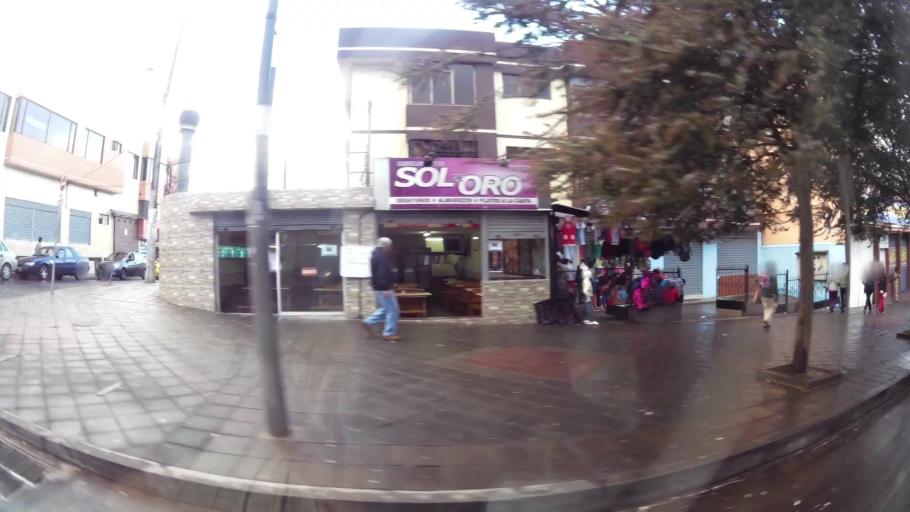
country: EC
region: Pichincha
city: Quito
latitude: -0.1145
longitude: -78.4967
